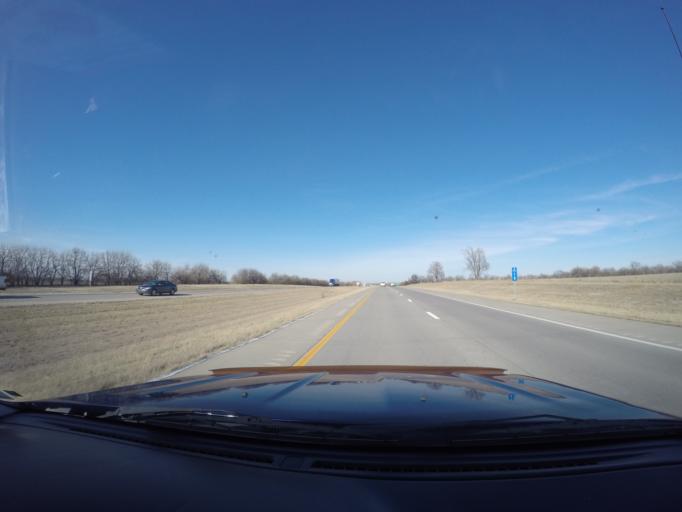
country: US
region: Kansas
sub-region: Sedgwick County
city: Valley Center
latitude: 37.8997
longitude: -97.3263
